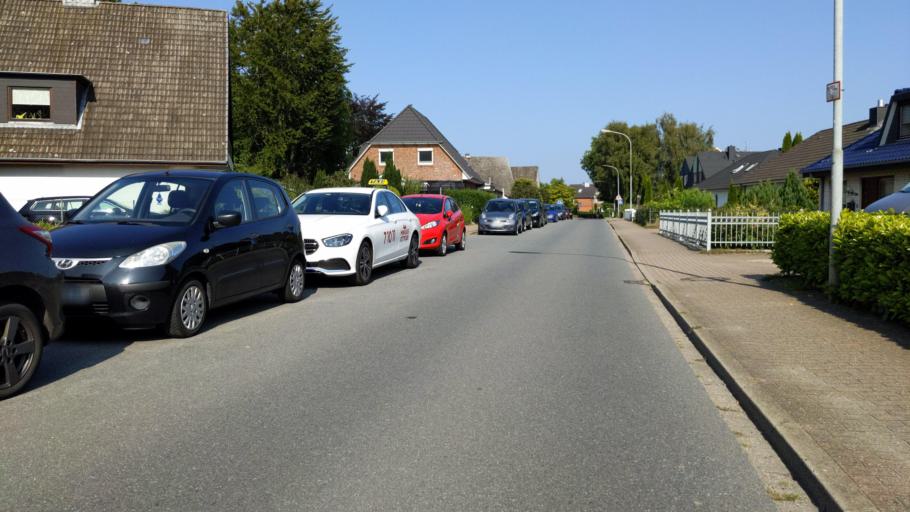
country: DE
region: Schleswig-Holstein
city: Stockelsdorf
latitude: 53.8839
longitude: 10.6394
